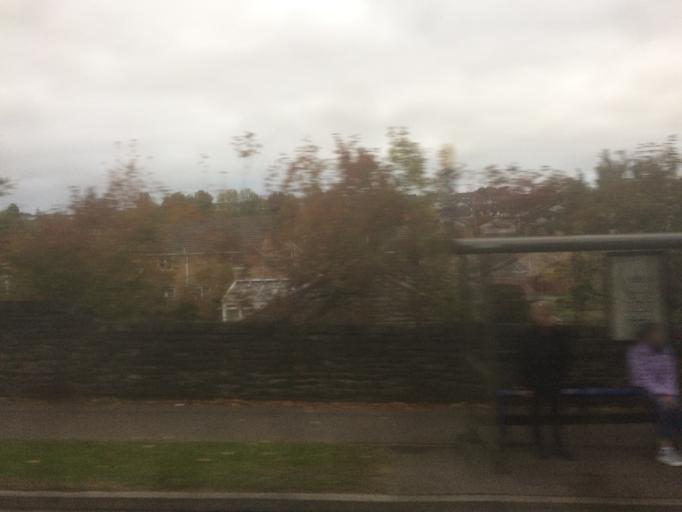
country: GB
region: Scotland
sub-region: Perth and Kinross
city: Perth
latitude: 56.3882
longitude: -3.4789
